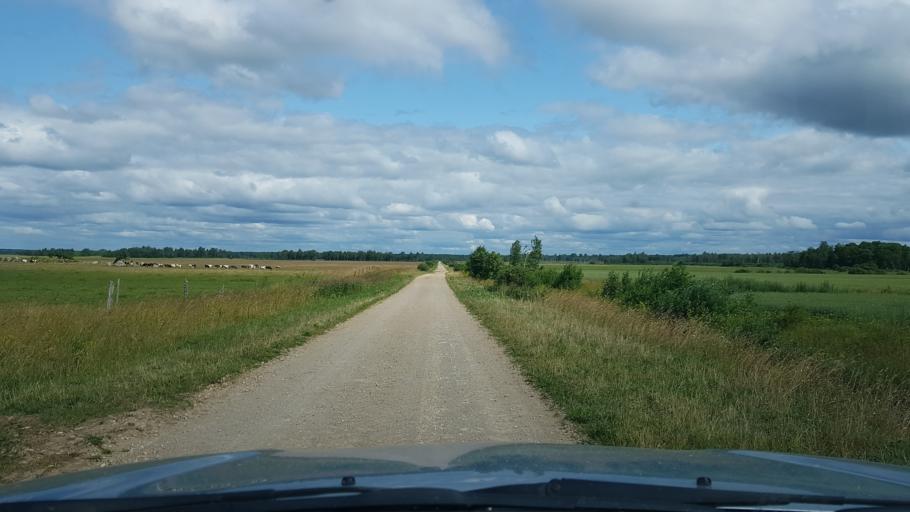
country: EE
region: Ida-Virumaa
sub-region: Sillamaee linn
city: Sillamae
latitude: 59.3703
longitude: 27.8892
